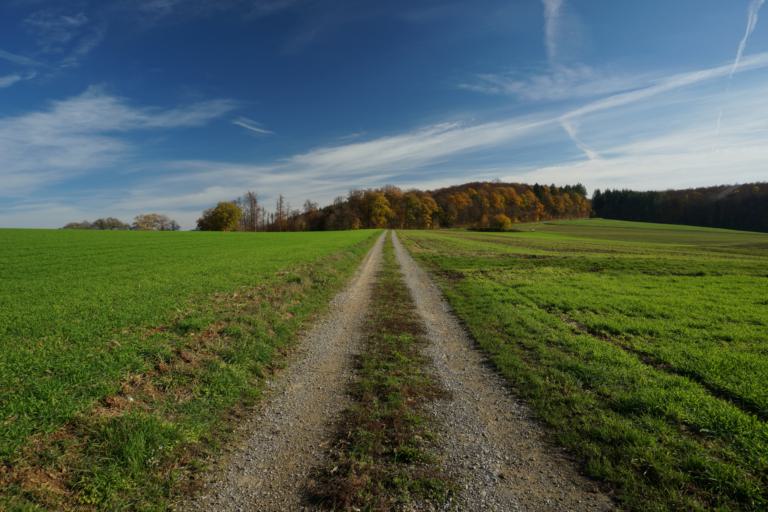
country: DE
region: Baden-Wuerttemberg
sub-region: Karlsruhe Region
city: Neunkirchen
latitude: 49.3606
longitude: 9.0191
